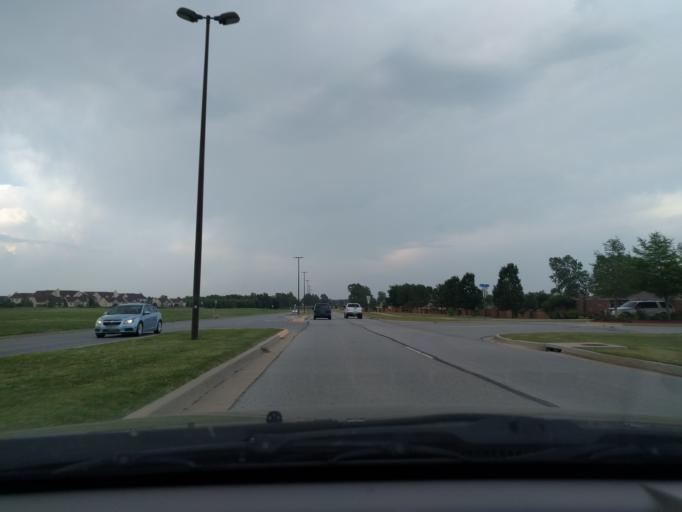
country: US
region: Oklahoma
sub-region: Tulsa County
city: Broken Arrow
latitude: 36.0742
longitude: -95.7868
